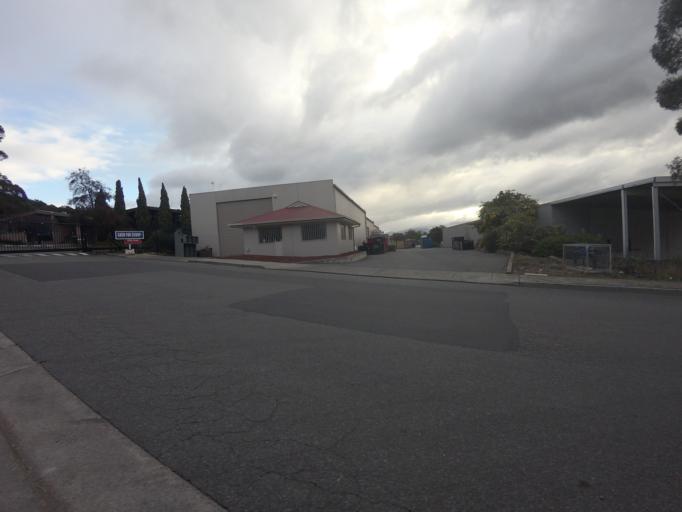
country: AU
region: Tasmania
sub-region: Clarence
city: Warrane
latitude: -42.8609
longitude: 147.3984
